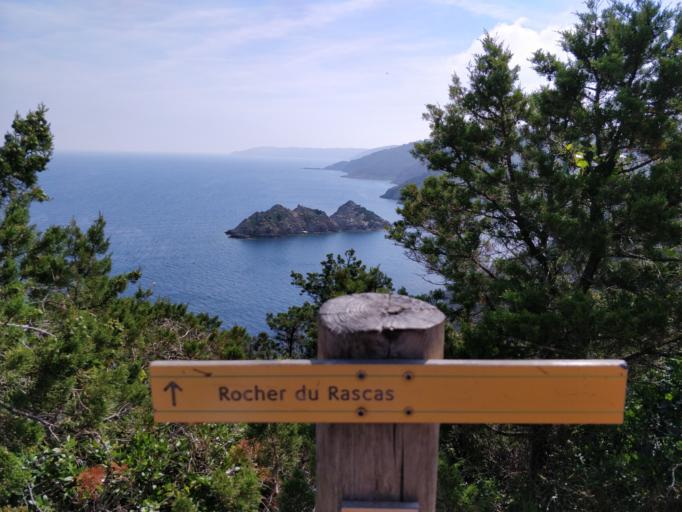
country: FR
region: Provence-Alpes-Cote d'Azur
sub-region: Departement du Var
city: Le Lavandou
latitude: 43.0130
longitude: 6.3840
